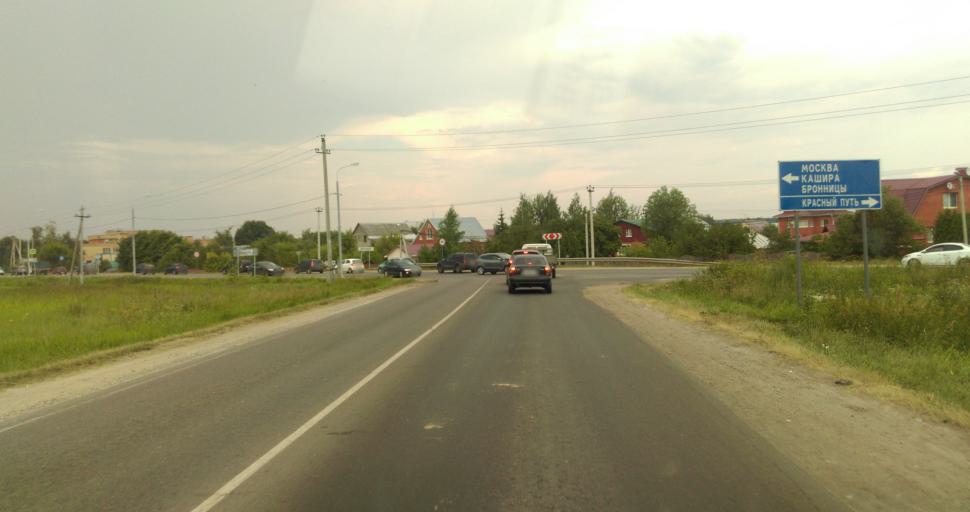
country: RU
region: Moskovskaya
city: Zhitnevo
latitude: 55.3378
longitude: 37.9091
